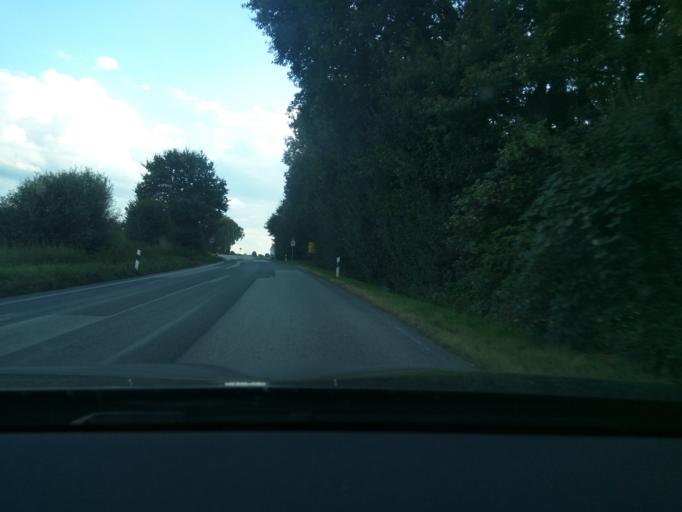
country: DE
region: Schleswig-Holstein
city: Kruzen
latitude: 53.4162
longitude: 10.5362
